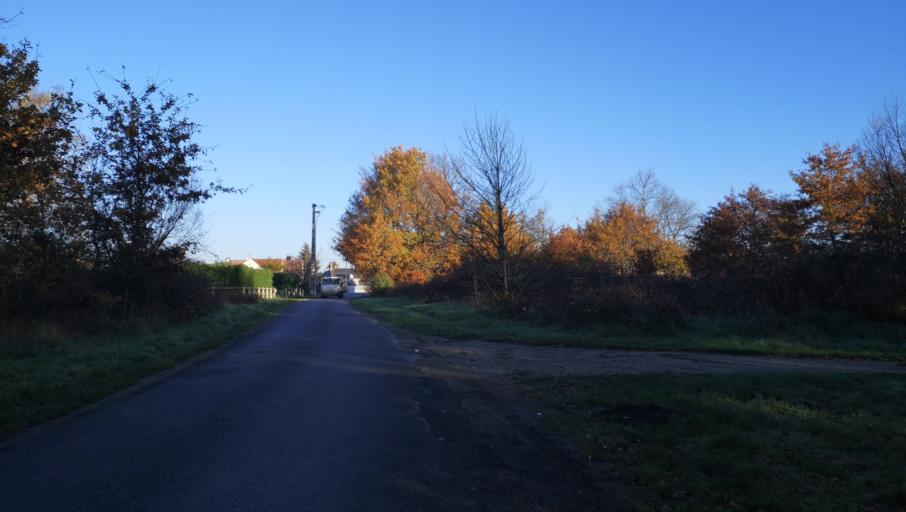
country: FR
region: Centre
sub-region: Departement du Loiret
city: Saint-Jean-de-la-Ruelle
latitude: 47.9295
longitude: 1.8612
